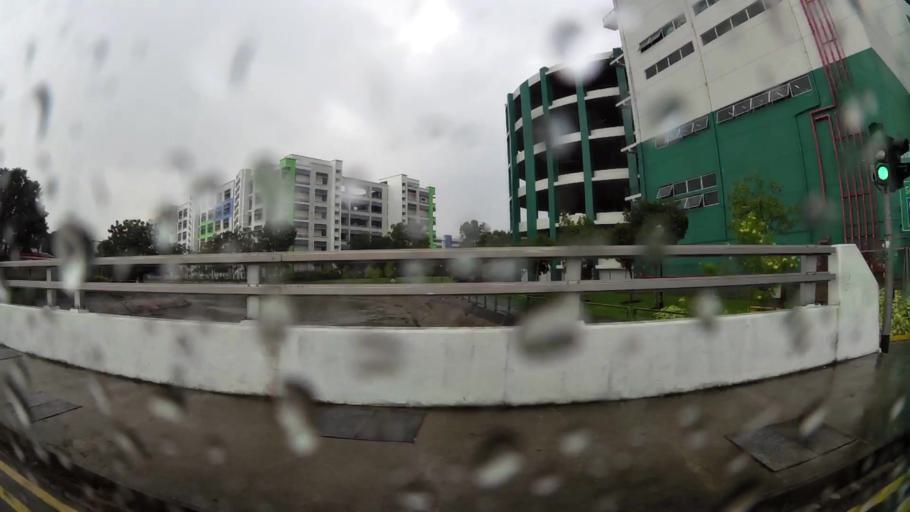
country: SG
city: Singapore
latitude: 1.3339
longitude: 103.9495
